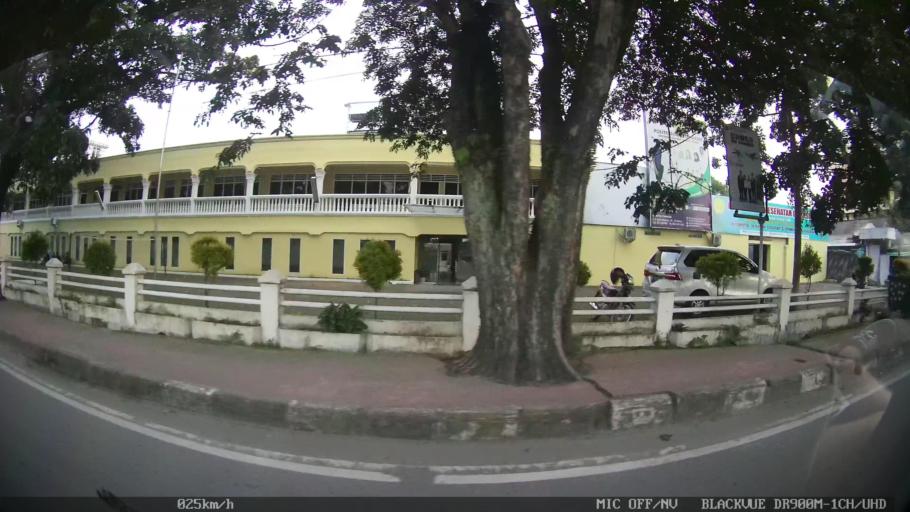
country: ID
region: North Sumatra
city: Medan
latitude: 3.6067
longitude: 98.6732
